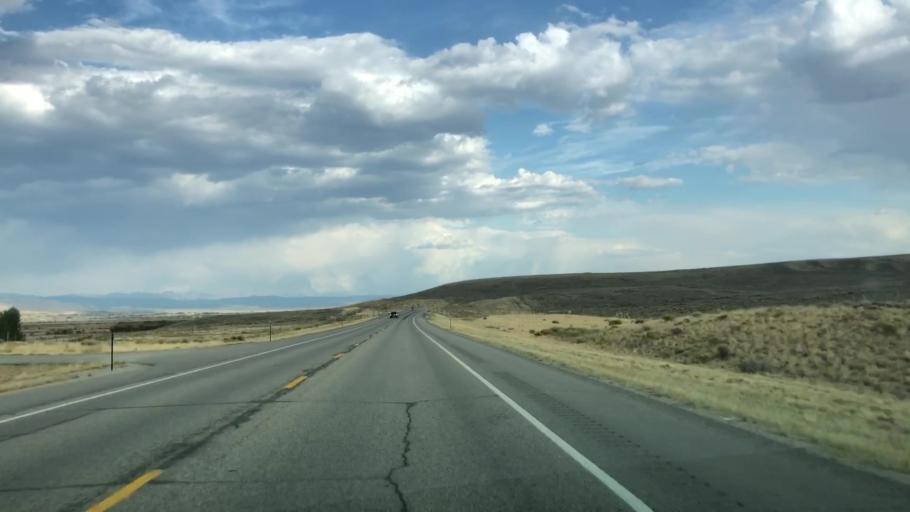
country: US
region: Wyoming
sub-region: Sublette County
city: Pinedale
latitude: 42.8762
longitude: -109.9567
